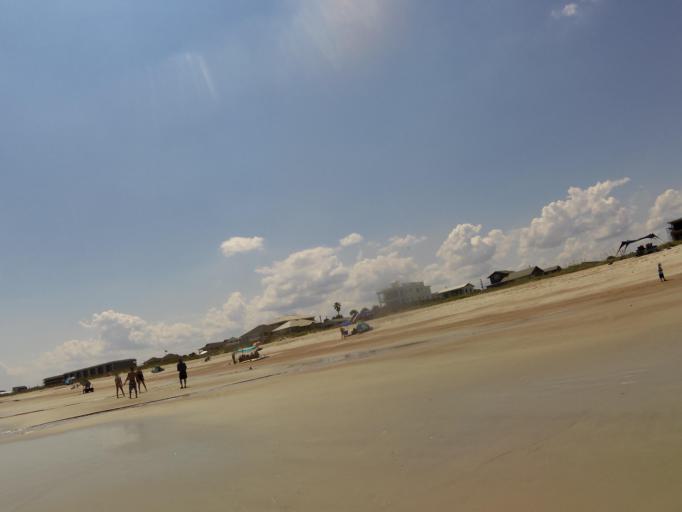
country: US
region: Florida
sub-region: Nassau County
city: Fernandina Beach
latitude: 30.6653
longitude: -81.4302
